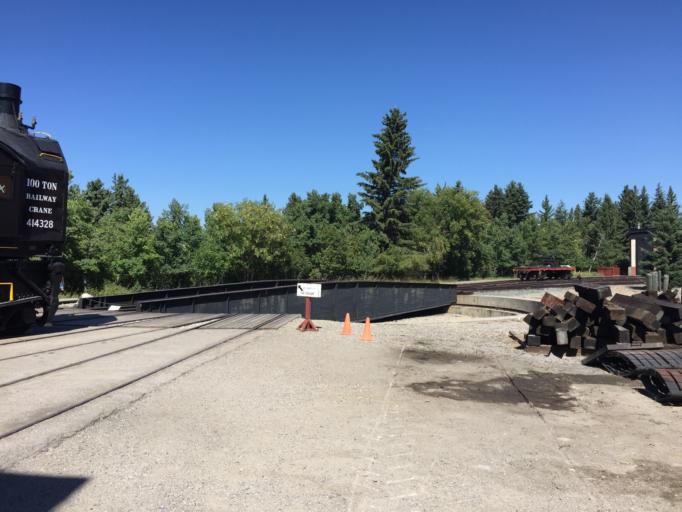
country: CA
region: Alberta
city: Calgary
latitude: 50.9855
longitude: -114.1095
